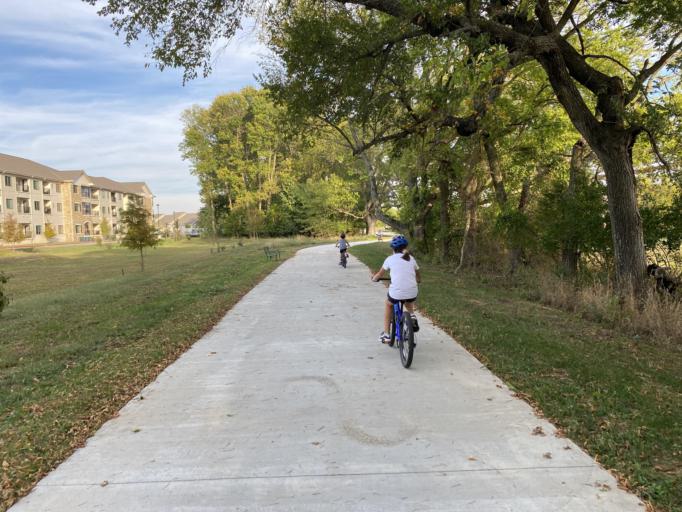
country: US
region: Arkansas
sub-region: Washington County
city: Johnson
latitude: 36.1104
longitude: -94.1885
